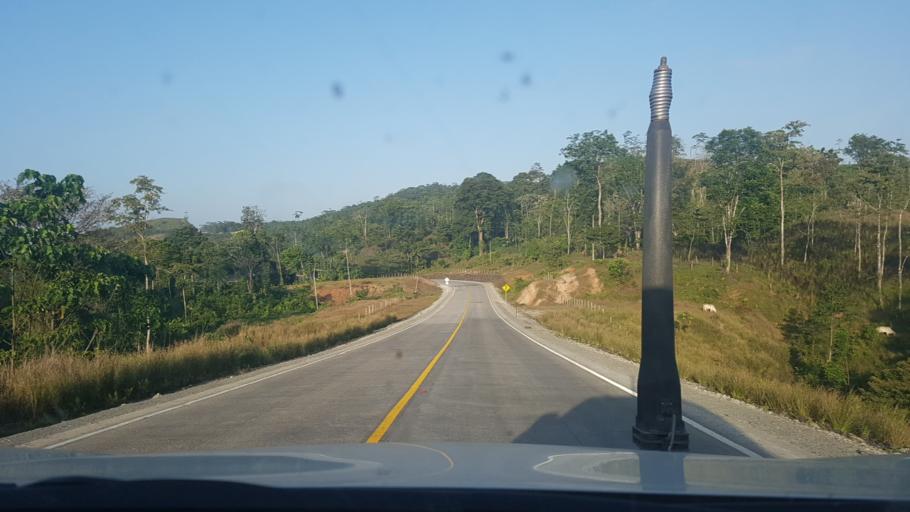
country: NI
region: Atlantico Sur
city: Rama
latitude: 11.8215
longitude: -84.0891
